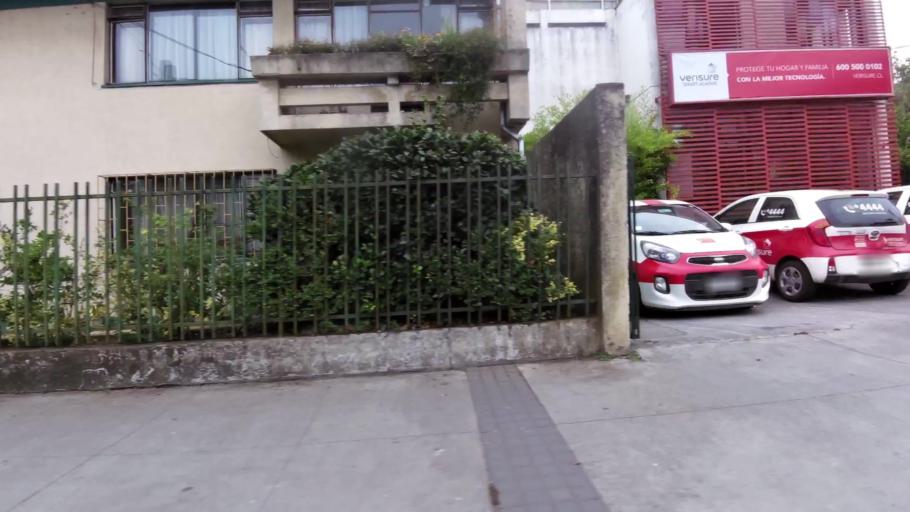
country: CL
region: Biobio
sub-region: Provincia de Concepcion
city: Concepcion
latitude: -36.8316
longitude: -73.0532
